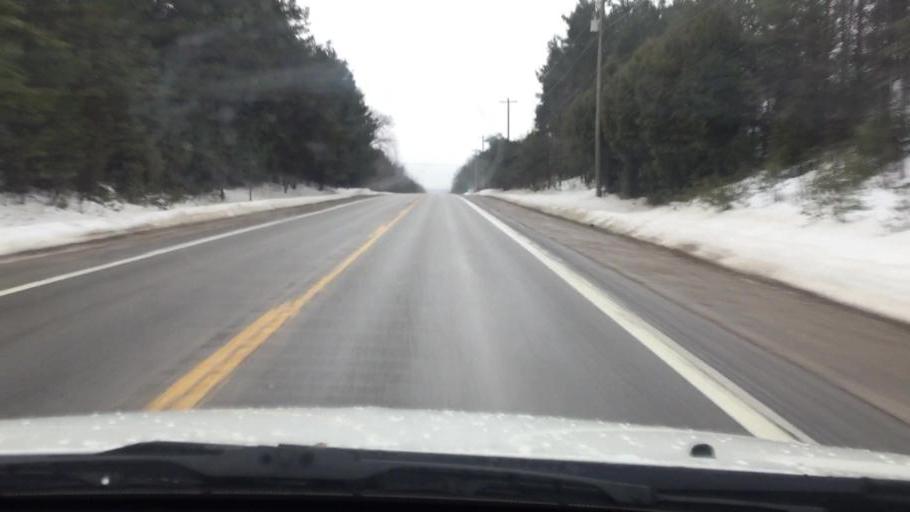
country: US
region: Michigan
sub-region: Charlevoix County
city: Charlevoix
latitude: 45.2666
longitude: -85.2034
